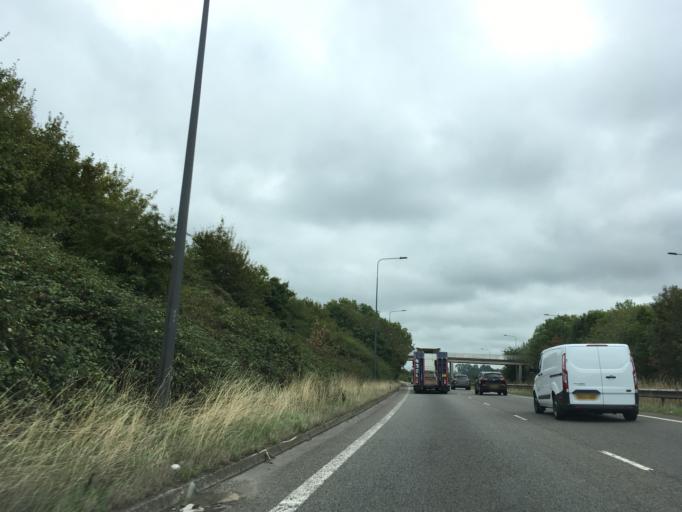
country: GB
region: England
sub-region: South Gloucestershire
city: Mangotsfield
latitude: 51.4961
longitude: -2.4761
